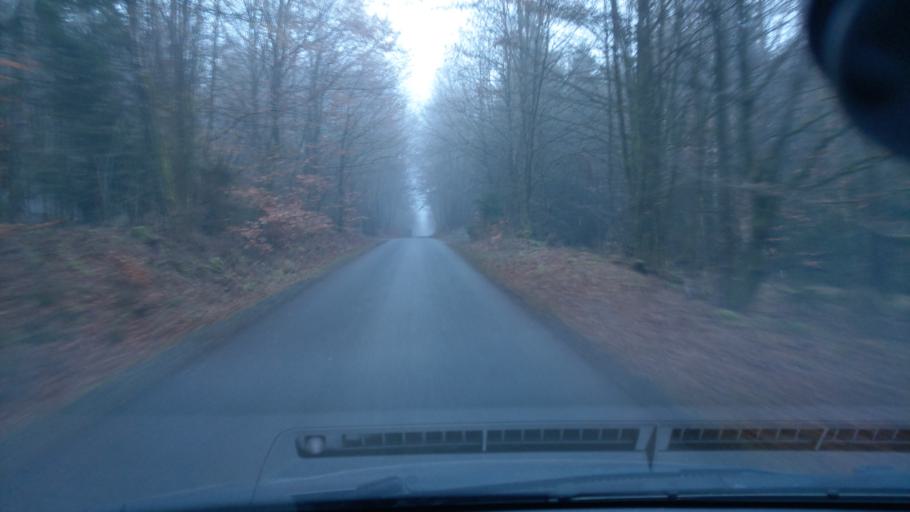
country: DE
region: Saarland
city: Tholey
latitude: 49.5097
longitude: 7.0145
